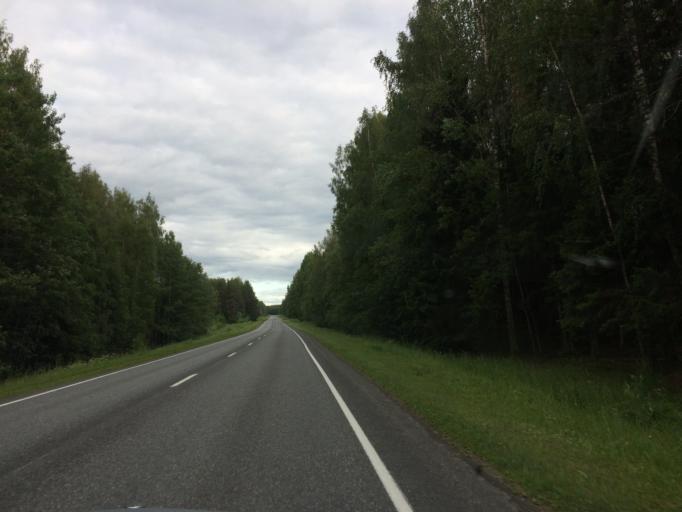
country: FI
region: Haeme
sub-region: Haemeenlinna
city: Haemeenlinna
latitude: 60.9369
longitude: 24.5233
